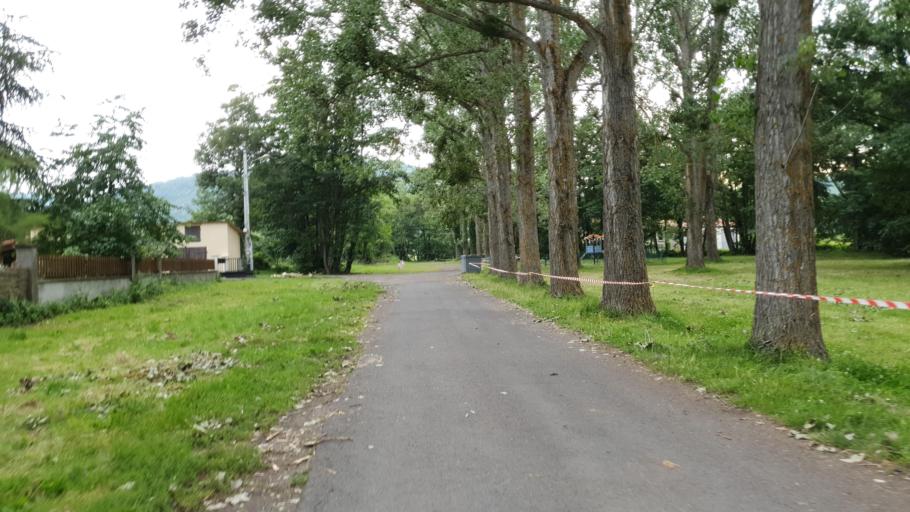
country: FR
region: Auvergne
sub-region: Departement du Puy-de-Dome
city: Aydat
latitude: 45.5724
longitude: 3.0128
